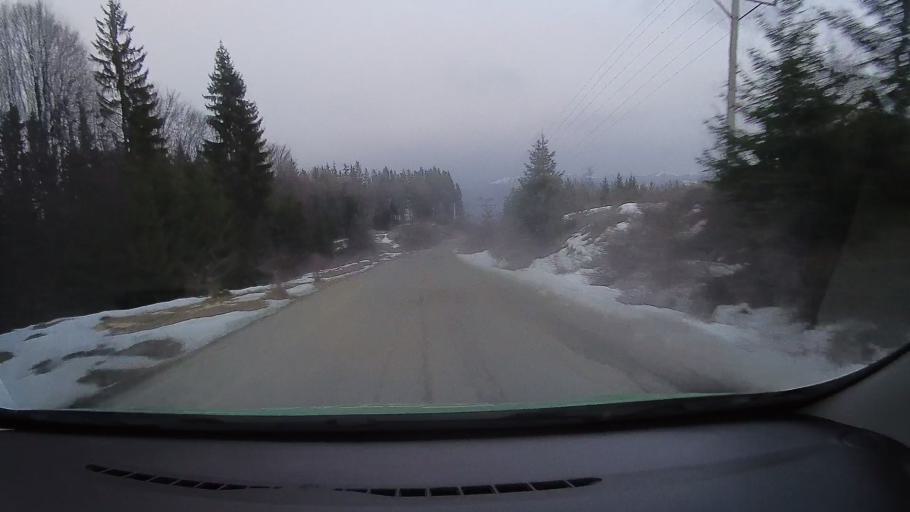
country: RO
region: Prahova
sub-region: Comuna Secaria
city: Secaria
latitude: 45.2895
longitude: 25.7030
